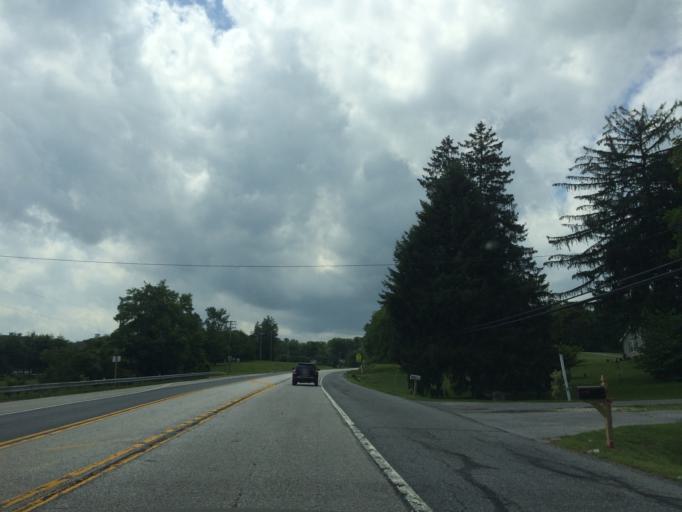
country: US
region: Maryland
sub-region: Carroll County
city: Eldersburg
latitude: 39.3949
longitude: -76.9113
